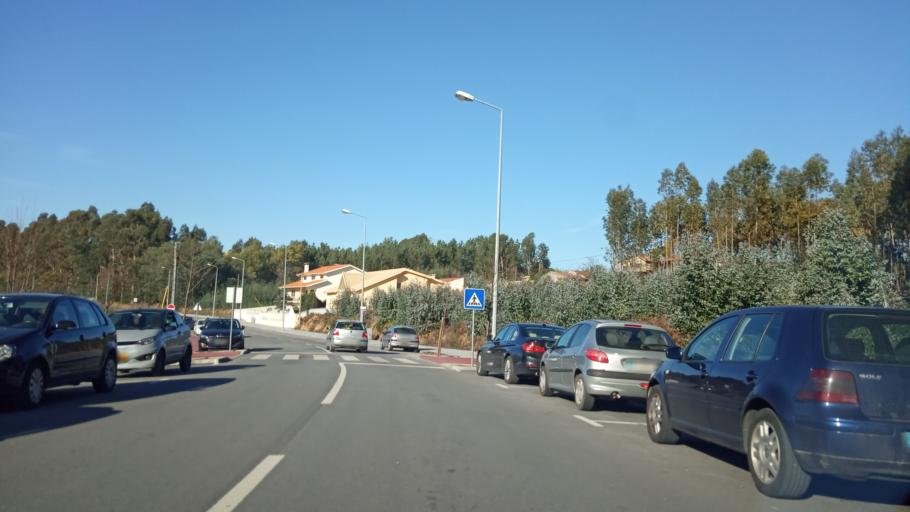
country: PT
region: Aveiro
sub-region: Anadia
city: Anadia
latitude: 40.4312
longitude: -8.4364
